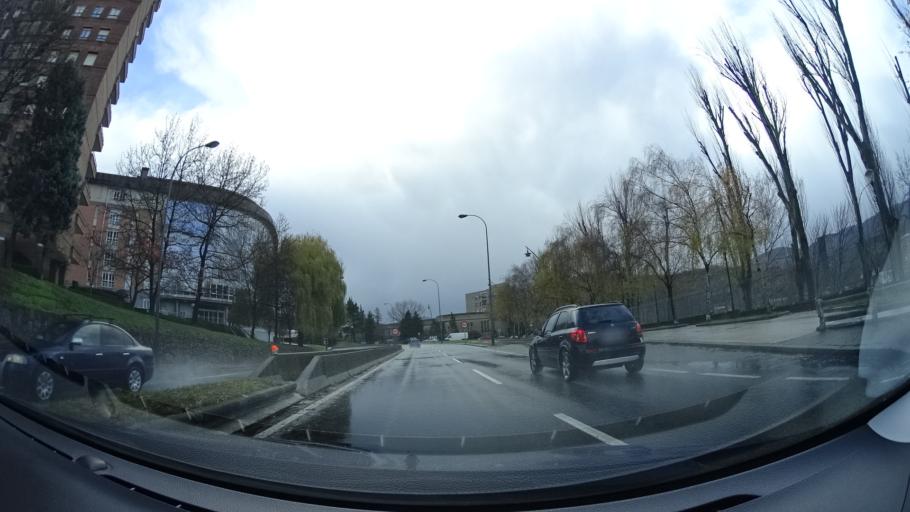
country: ES
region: Basque Country
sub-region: Bizkaia
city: Santutxu
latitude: 43.2504
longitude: -2.9062
